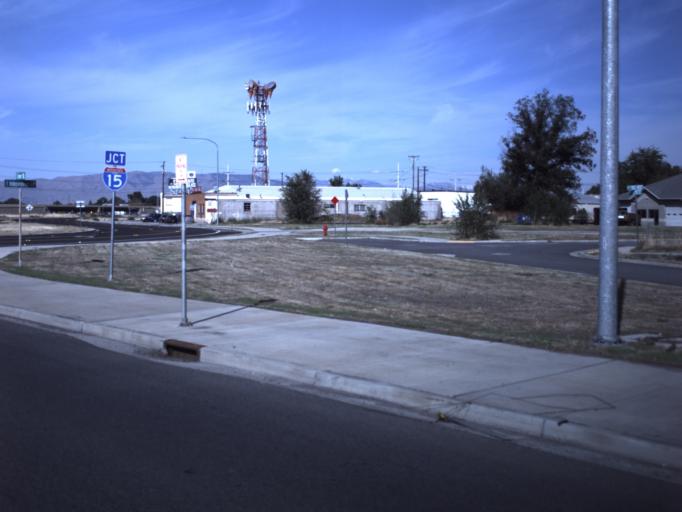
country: US
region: Utah
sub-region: Utah County
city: Provo
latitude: 40.2338
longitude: -111.6774
